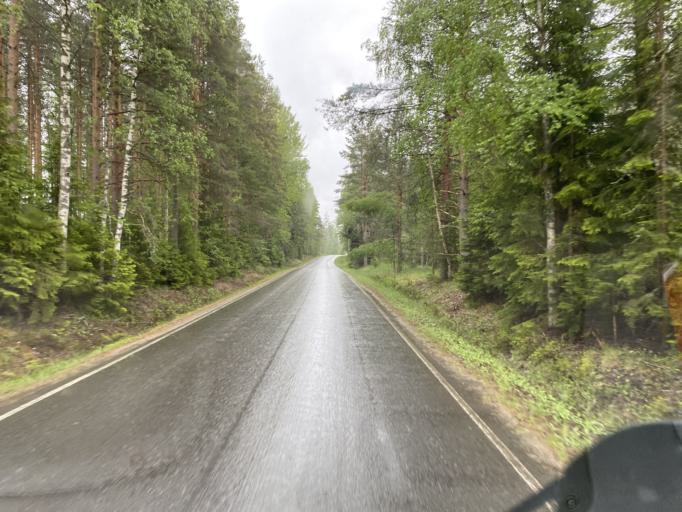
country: FI
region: Haeme
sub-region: Forssa
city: Humppila
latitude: 61.0850
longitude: 23.3101
